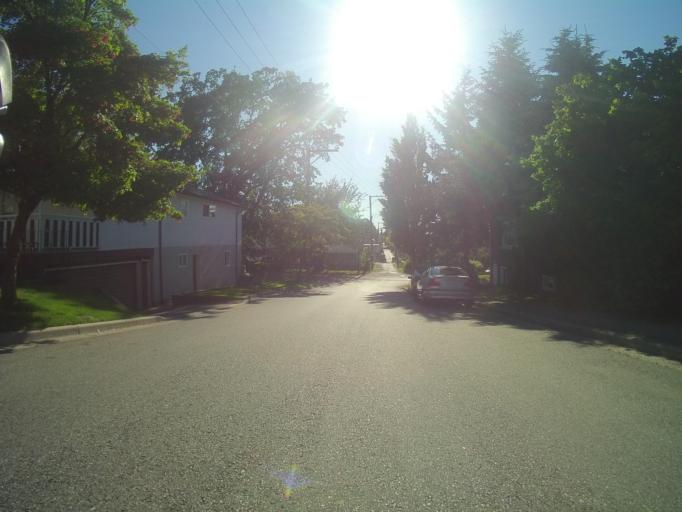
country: CA
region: British Columbia
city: Vancouver
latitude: 49.2429
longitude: -123.0661
